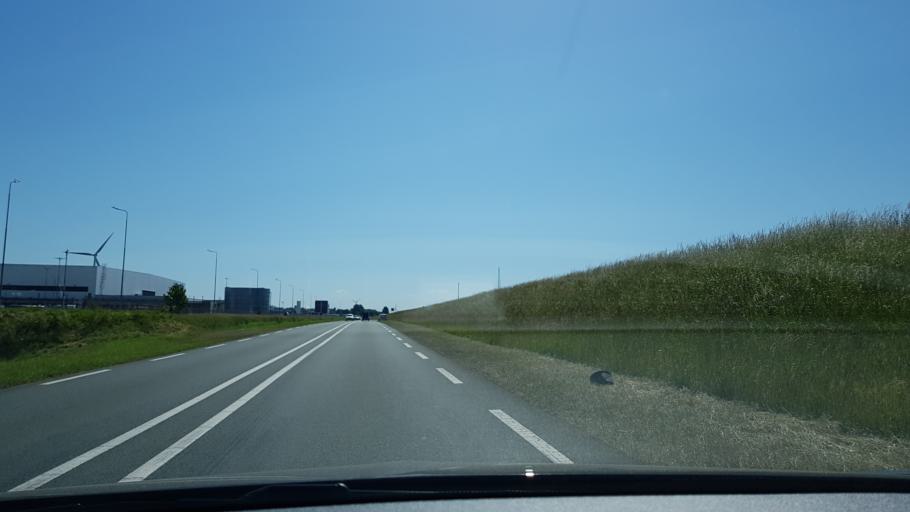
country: NL
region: North Holland
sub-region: Gemeente Zaanstad
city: Zaandam
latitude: 52.4252
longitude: 4.7968
